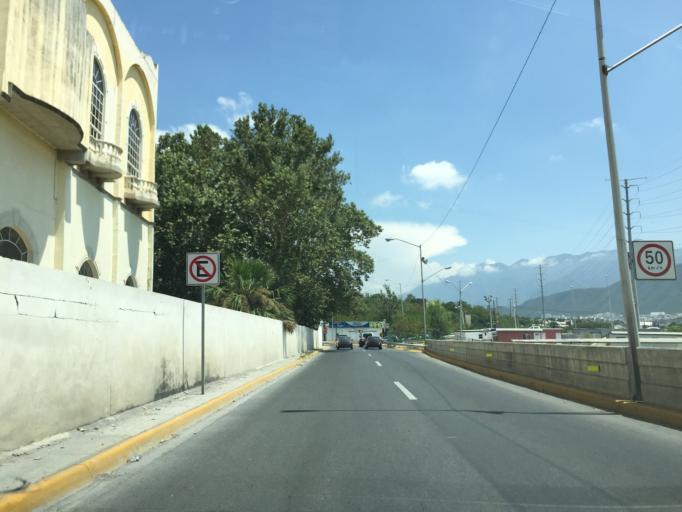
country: MX
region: Nuevo Leon
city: Guadalupe
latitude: 25.6404
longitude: -100.2686
